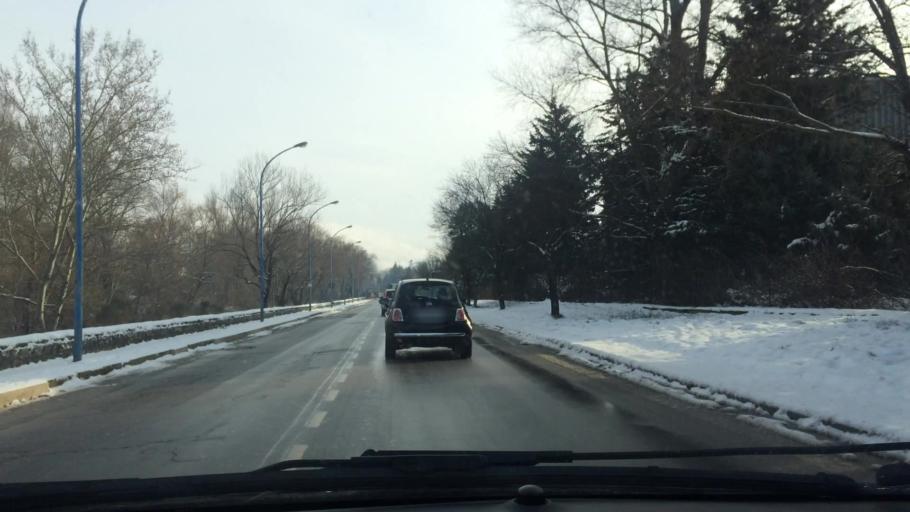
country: IT
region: Basilicate
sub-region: Provincia di Potenza
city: Potenza
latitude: 40.6294
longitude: 15.8106
